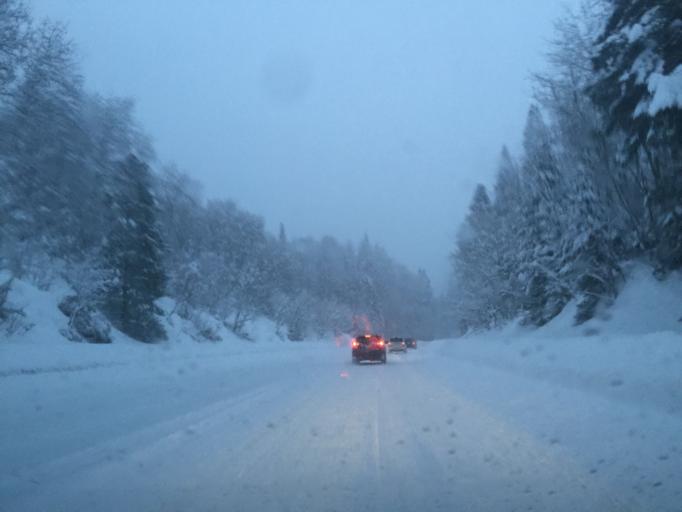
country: US
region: Washington
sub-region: Chelan County
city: Leavenworth
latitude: 47.7899
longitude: -120.8628
